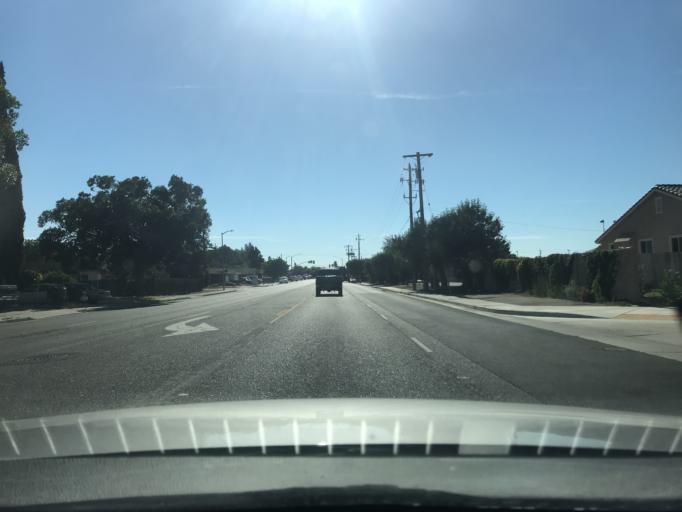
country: US
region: California
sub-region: Merced County
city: Atwater
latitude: 37.3499
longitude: -120.5931
